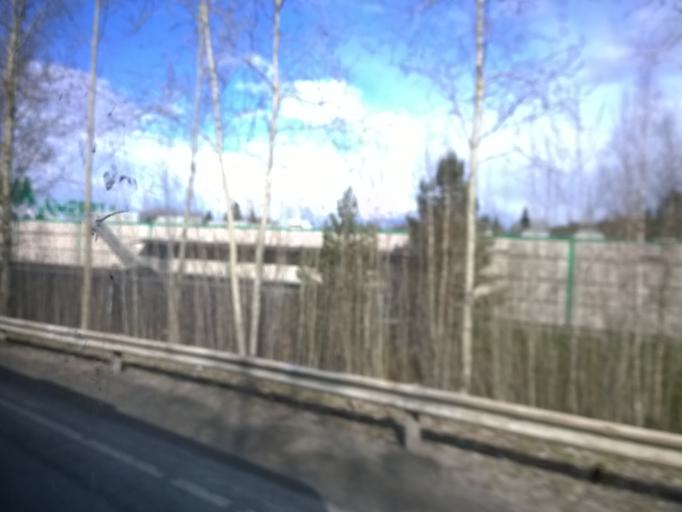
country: FI
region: Pirkanmaa
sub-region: Tampere
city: Tampere
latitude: 61.4680
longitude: 23.7751
